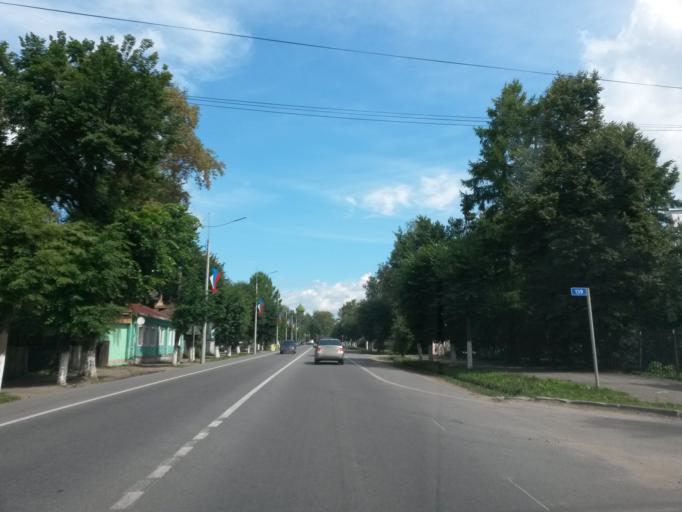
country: RU
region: Jaroslavl
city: Pereslavl'-Zalesskiy
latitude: 56.7315
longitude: 38.8482
